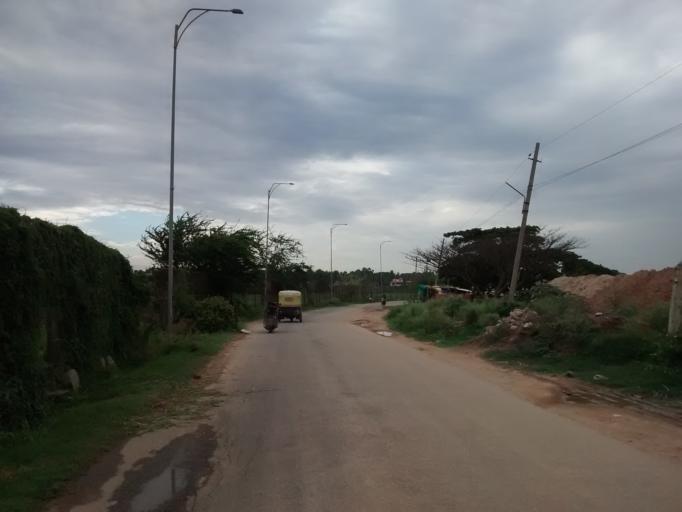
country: IN
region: Karnataka
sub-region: Bangalore Urban
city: Bangalore
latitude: 12.9371
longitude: 77.6772
